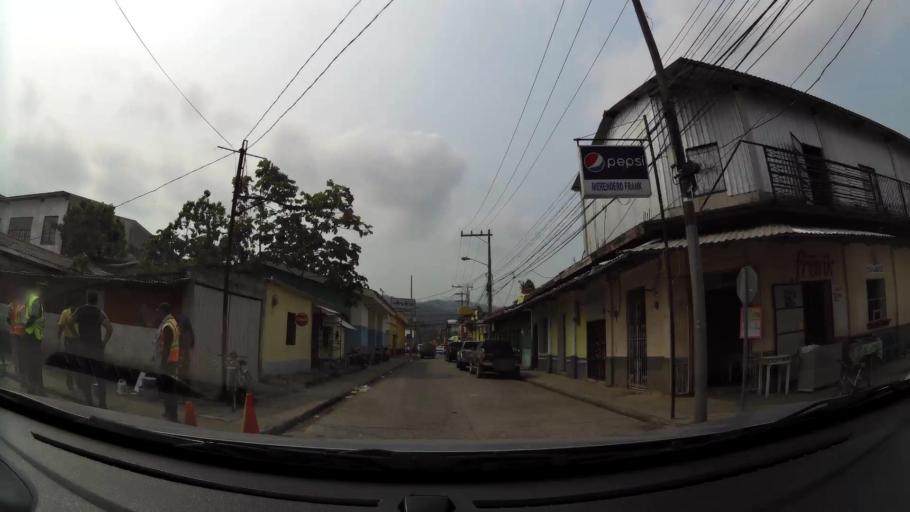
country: HN
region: Atlantida
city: Tela
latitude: 15.7829
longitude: -87.4532
